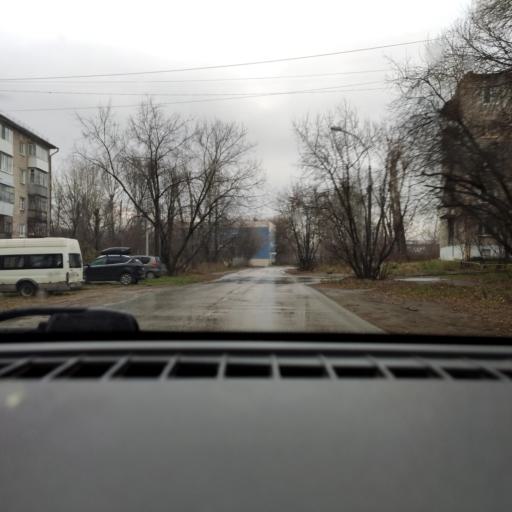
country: RU
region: Perm
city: Kultayevo
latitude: 57.9979
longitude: 55.9352
